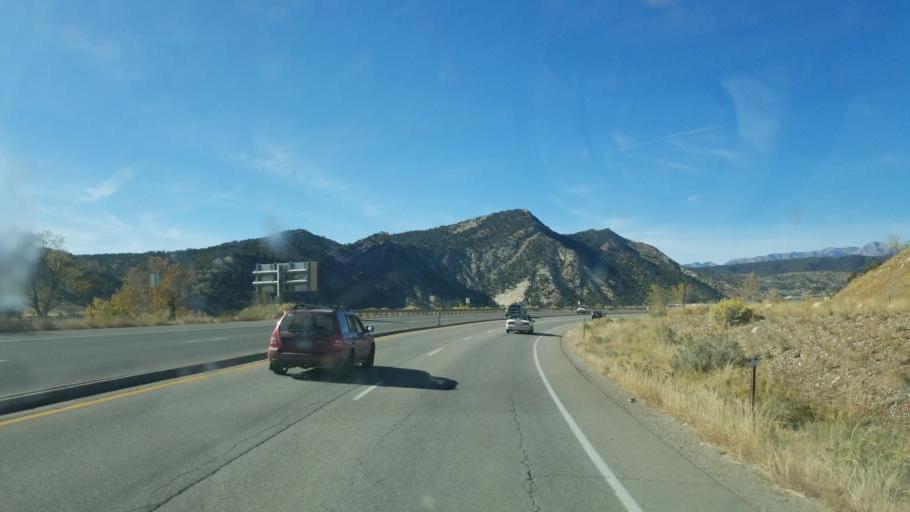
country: US
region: Colorado
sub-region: La Plata County
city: Durango
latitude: 37.2197
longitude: -107.8527
